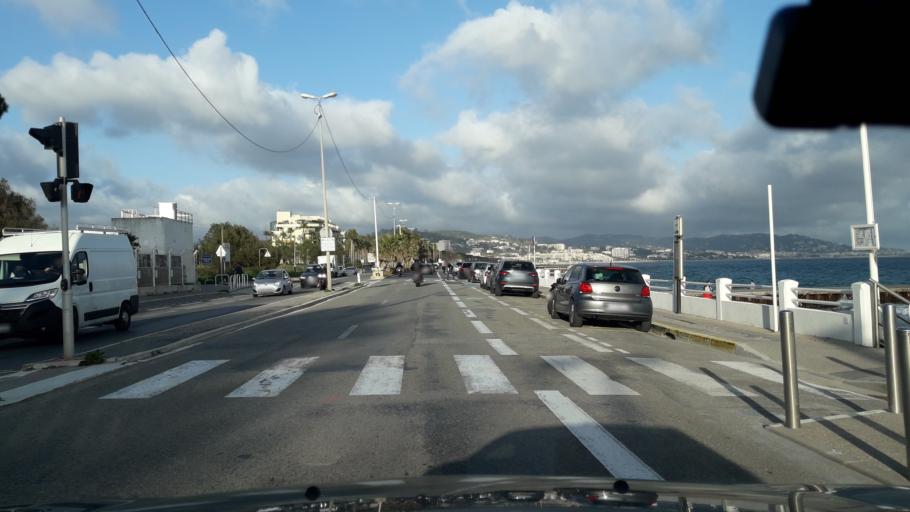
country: FR
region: Provence-Alpes-Cote d'Azur
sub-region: Departement des Alpes-Maritimes
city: Mandelieu-la-Napoule
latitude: 43.5386
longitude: 6.9563
